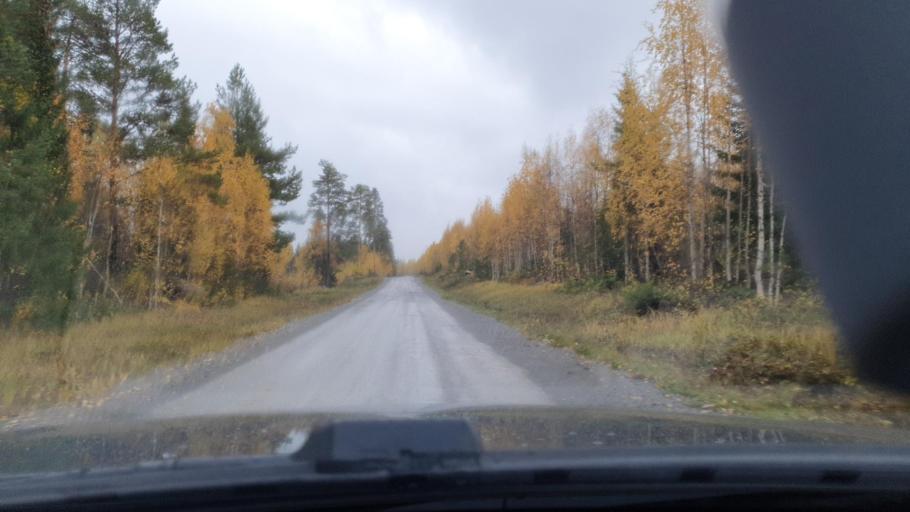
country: SE
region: Jaemtland
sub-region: Stroemsunds Kommun
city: Stroemsund
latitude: 63.5471
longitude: 15.5573
